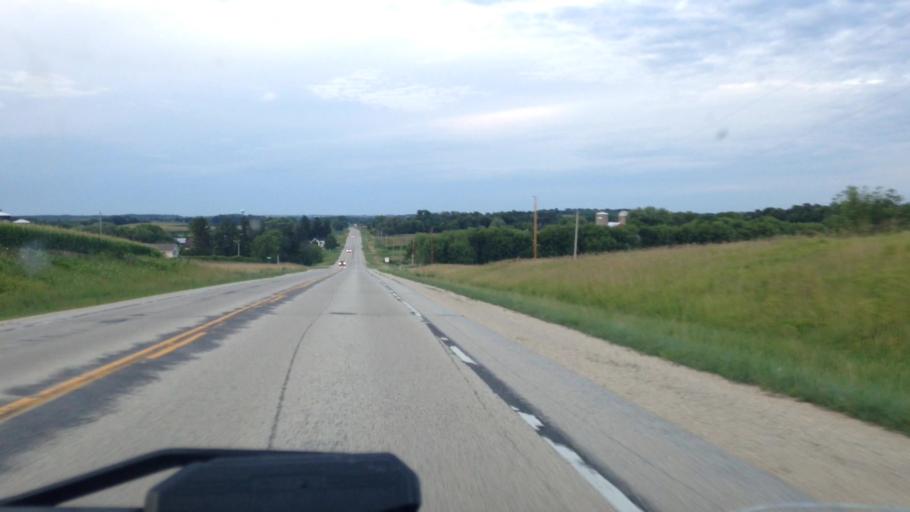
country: US
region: Wisconsin
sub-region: Dodge County
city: Theresa
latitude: 43.4842
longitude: -88.4501
